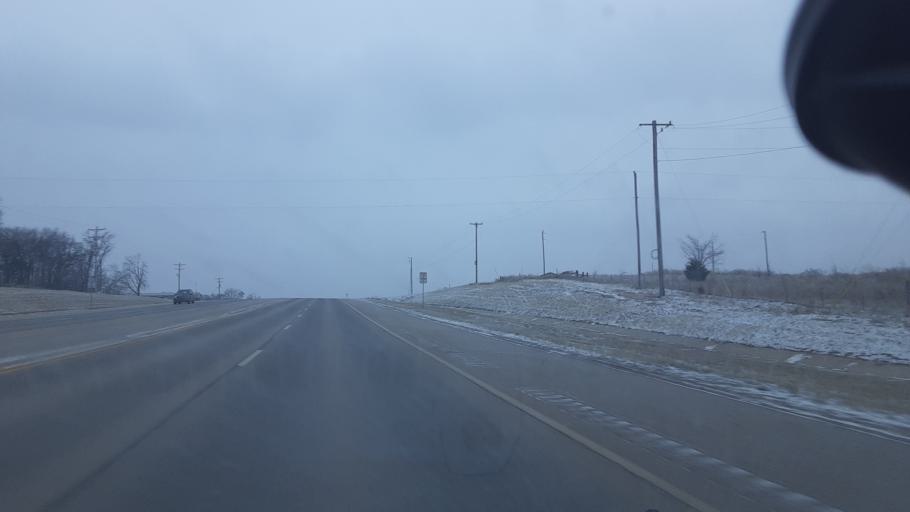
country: US
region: Oklahoma
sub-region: Payne County
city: Perkins
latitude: 35.9856
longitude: -97.0583
